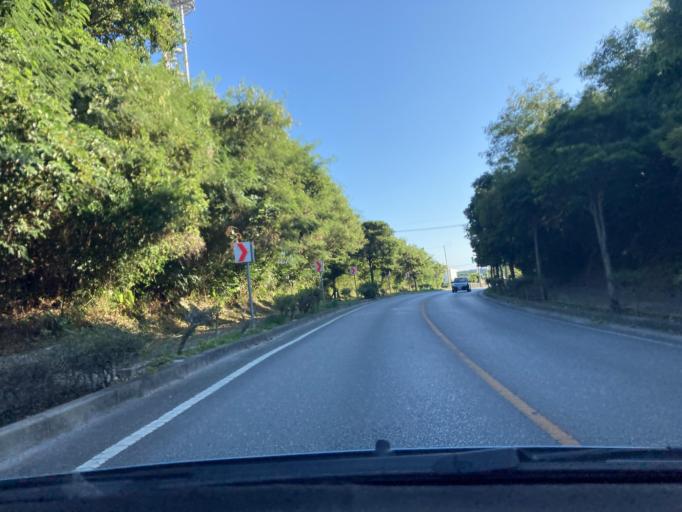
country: JP
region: Okinawa
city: Itoman
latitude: 26.1037
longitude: 127.6782
